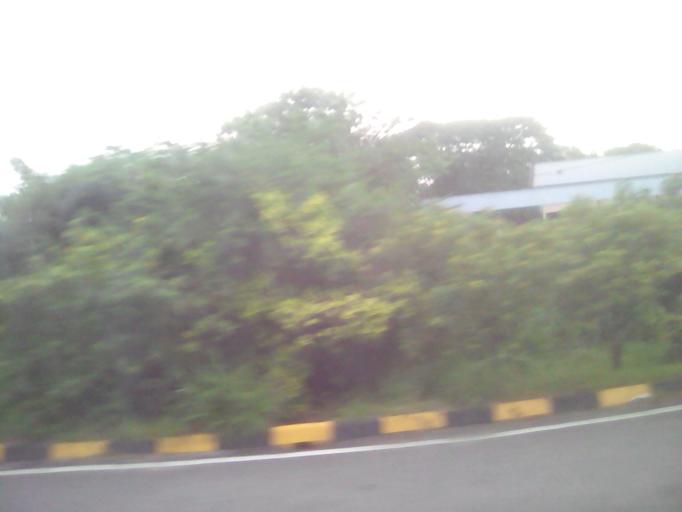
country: MY
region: Penang
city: Butterworth
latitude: 5.4056
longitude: 100.3764
